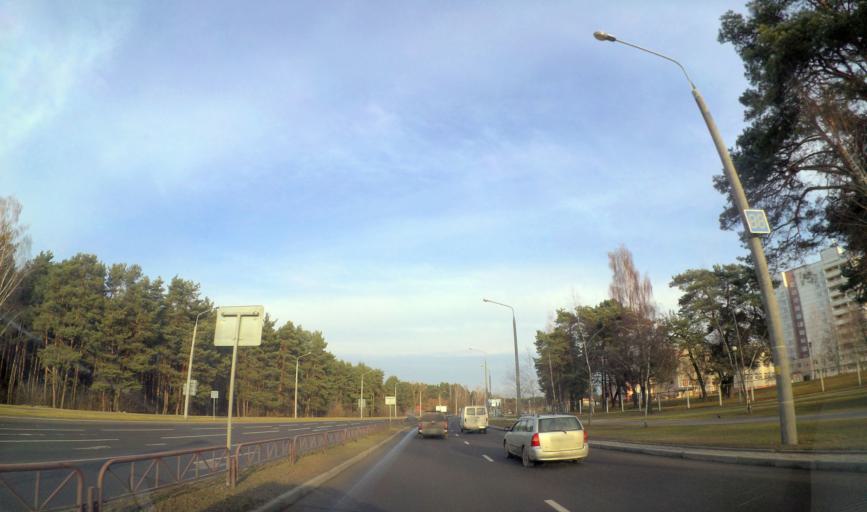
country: BY
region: Grodnenskaya
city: Hrodna
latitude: 53.6734
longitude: 23.7945
